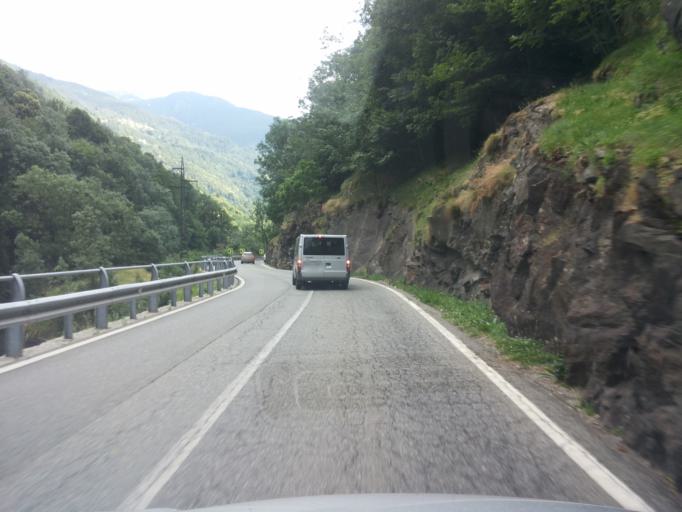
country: IT
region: Aosta Valley
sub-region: Valle d'Aosta
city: Issime
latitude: 45.6681
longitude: 7.8585
